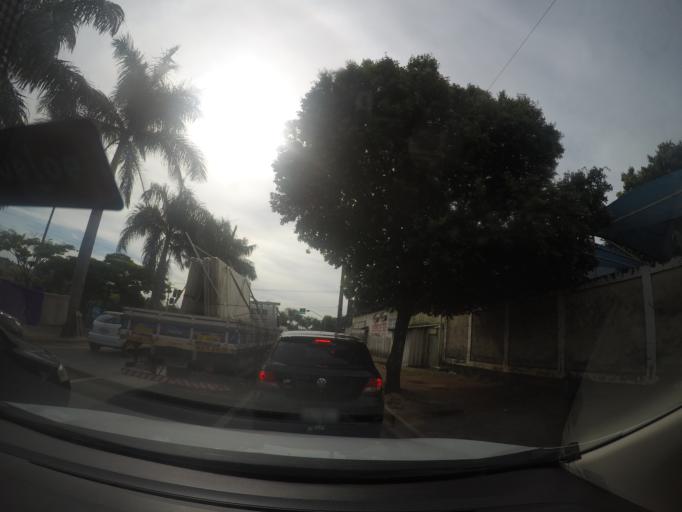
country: BR
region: Goias
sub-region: Goiania
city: Goiania
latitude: -16.6557
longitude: -49.3003
